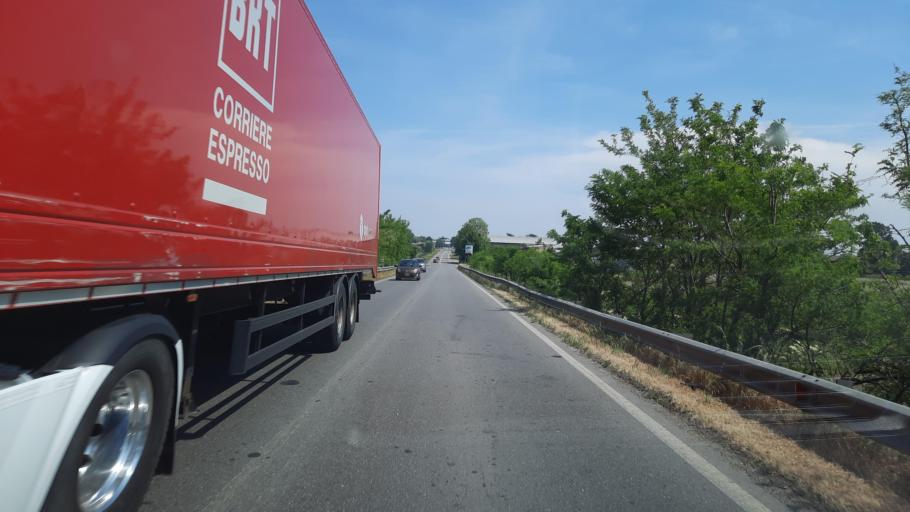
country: IT
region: Lombardy
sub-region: Provincia di Pavia
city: Mortara
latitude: 45.2458
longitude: 8.7307
